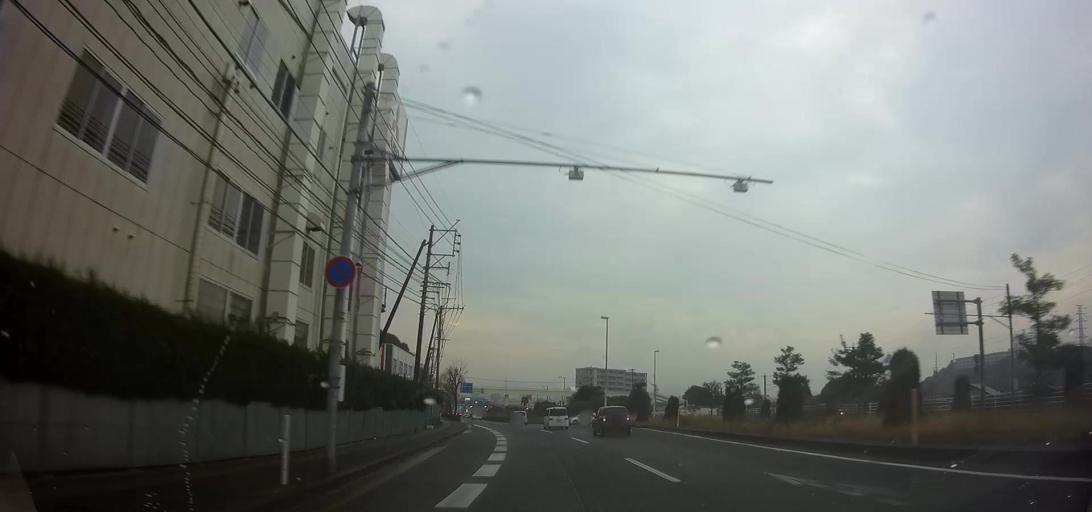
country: JP
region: Nagasaki
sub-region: Isahaya-shi
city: Isahaya
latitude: 32.8410
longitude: 130.0278
